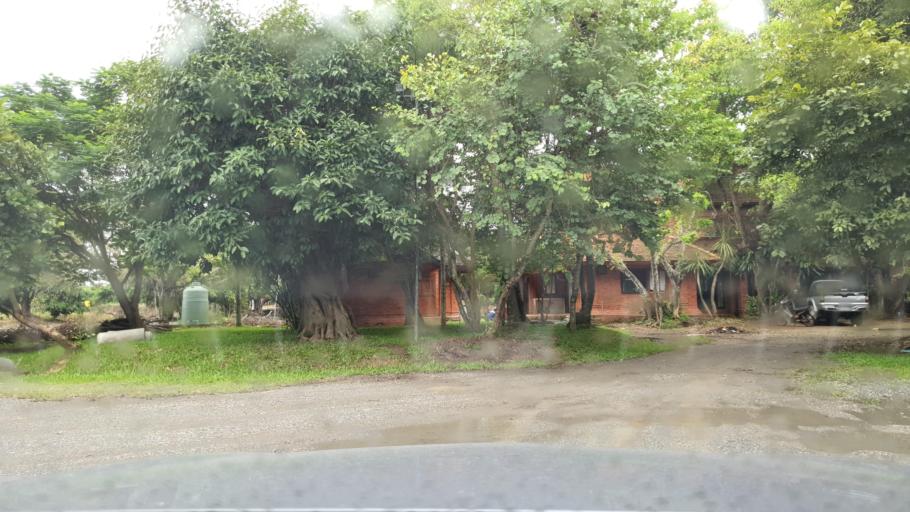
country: TH
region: Lamphun
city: Lamphun
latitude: 18.6053
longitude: 98.9773
